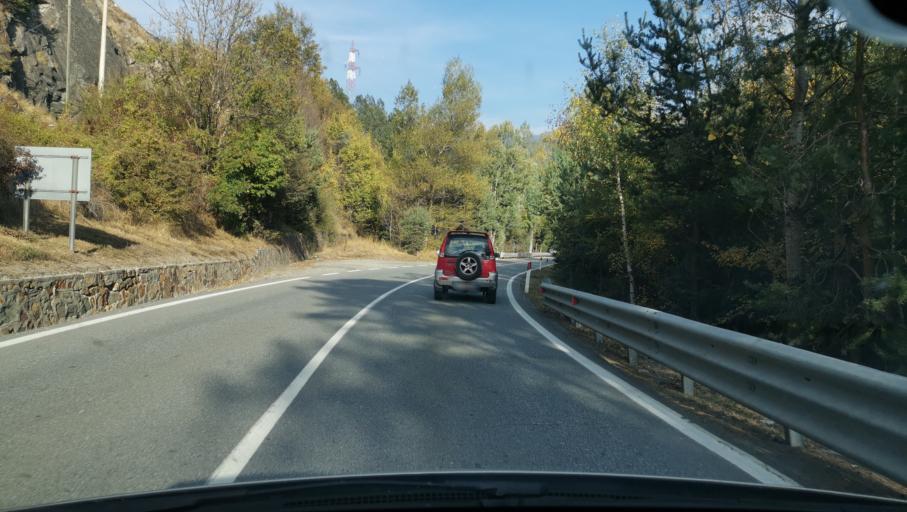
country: IT
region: Piedmont
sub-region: Provincia di Torino
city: Oulx
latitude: 45.0422
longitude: 6.8264
